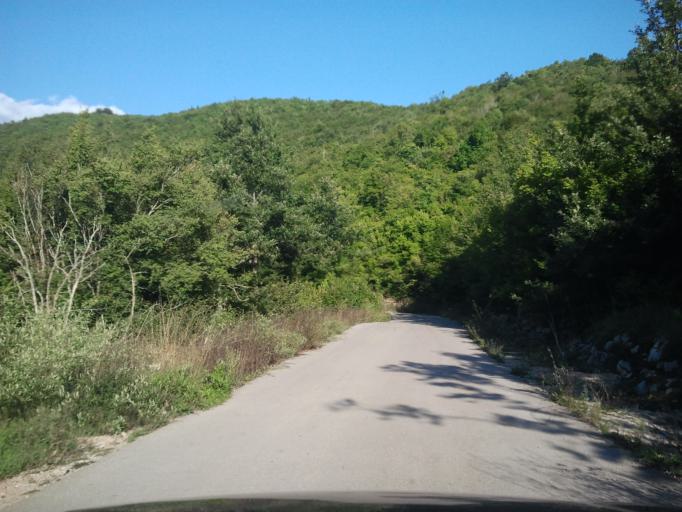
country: HR
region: Zadarska
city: Gracac
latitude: 44.3667
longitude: 15.7019
